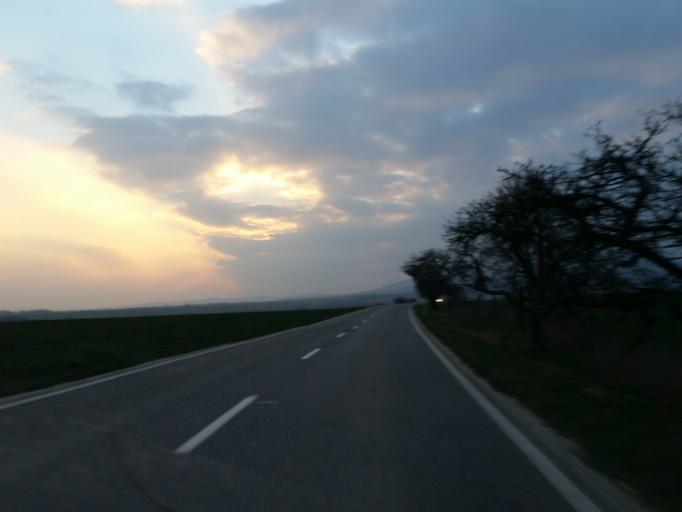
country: SK
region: Nitriansky
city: Banovce nad Bebravou
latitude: 48.5683
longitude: 18.0858
